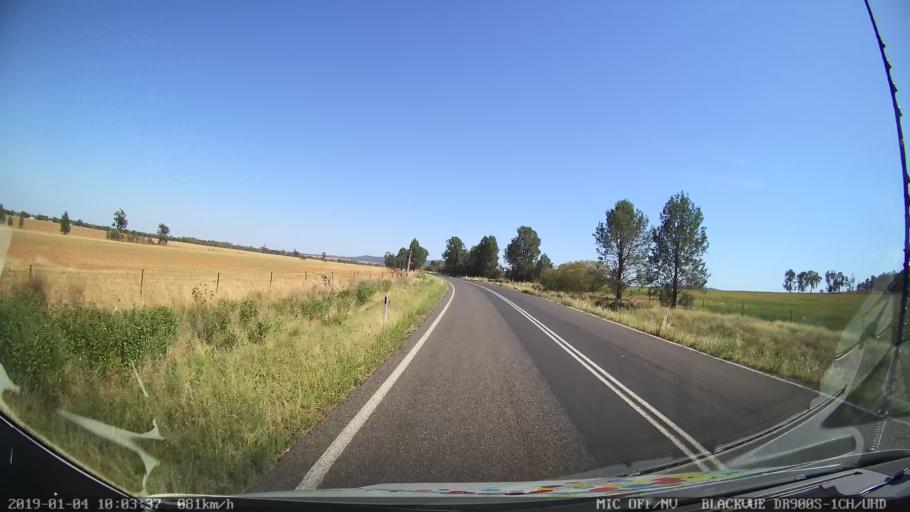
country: AU
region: New South Wales
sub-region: Cabonne
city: Canowindra
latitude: -33.4617
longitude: 148.3640
